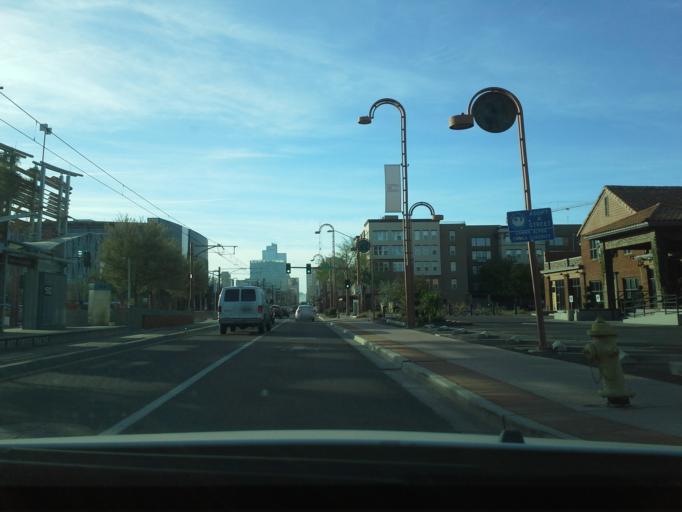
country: US
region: Arizona
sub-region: Maricopa County
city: Phoenix
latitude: 33.4647
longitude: -112.0739
